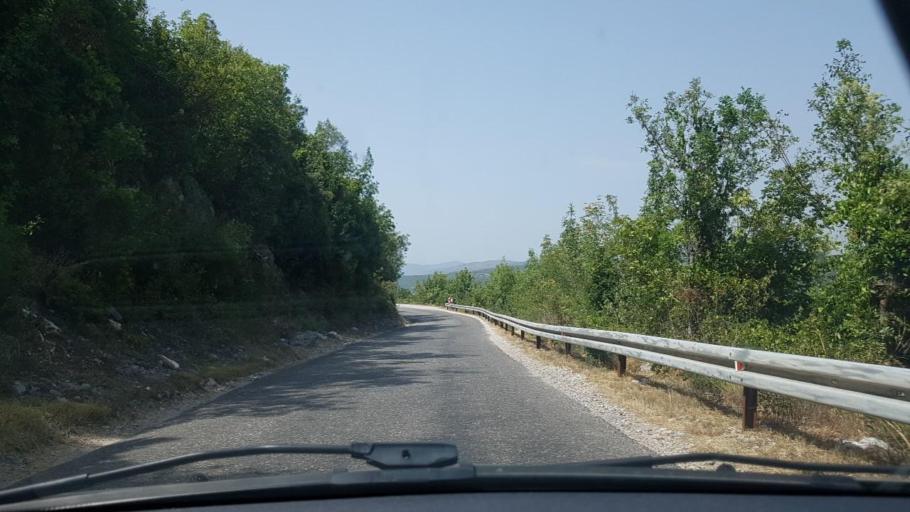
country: BA
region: Federation of Bosnia and Herzegovina
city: Tasovcici
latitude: 43.0127
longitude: 17.7879
